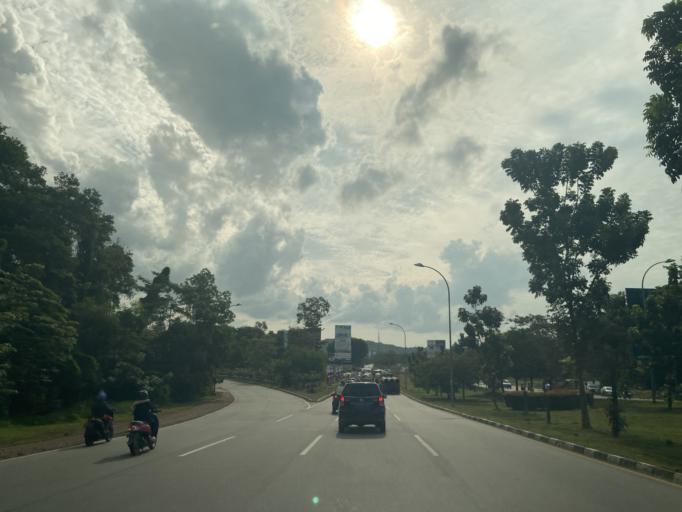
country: SG
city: Singapore
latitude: 1.1015
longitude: 104.0409
